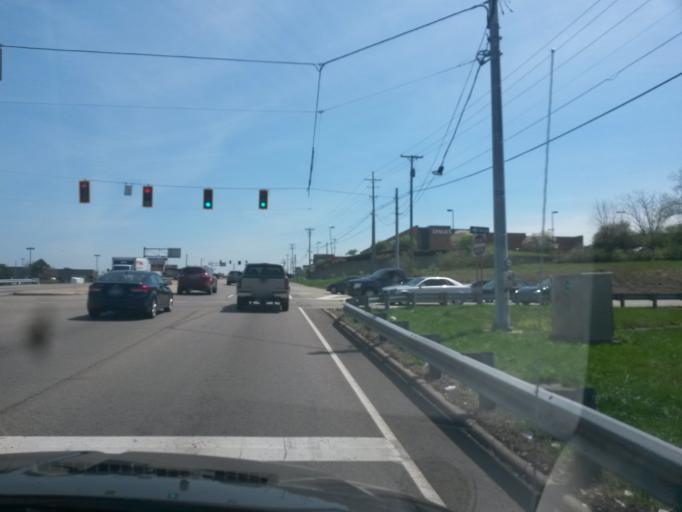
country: US
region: Ohio
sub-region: Montgomery County
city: West Carrollton City
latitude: 39.6391
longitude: -84.2305
